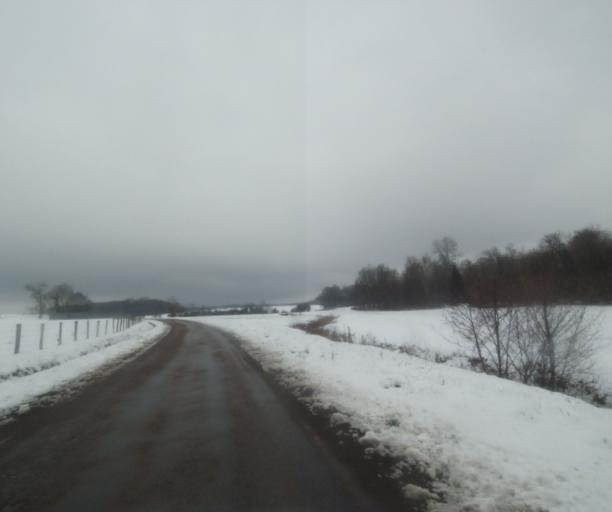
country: FR
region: Champagne-Ardenne
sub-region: Departement de la Haute-Marne
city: Laneuville-a-Remy
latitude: 48.4622
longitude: 4.8309
